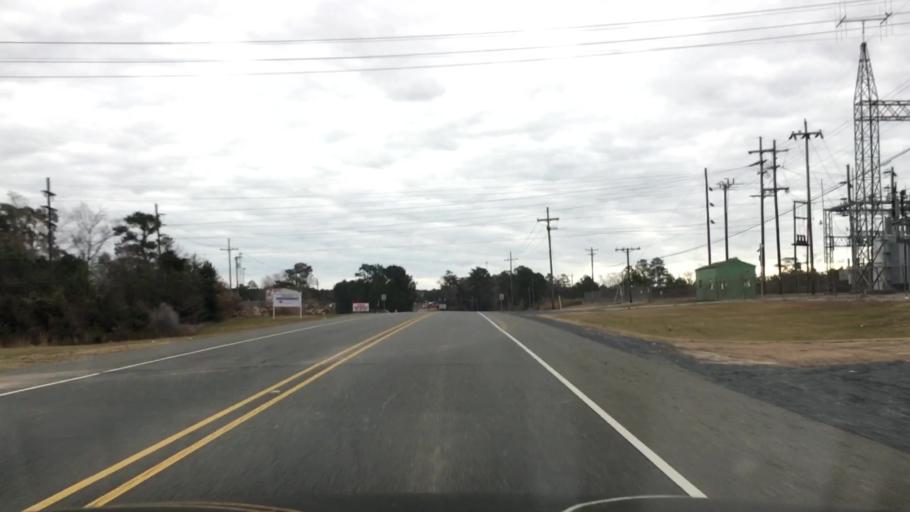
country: US
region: Louisiana
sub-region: Vernon Parish
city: Fort Polk South
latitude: 31.0566
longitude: -93.2531
